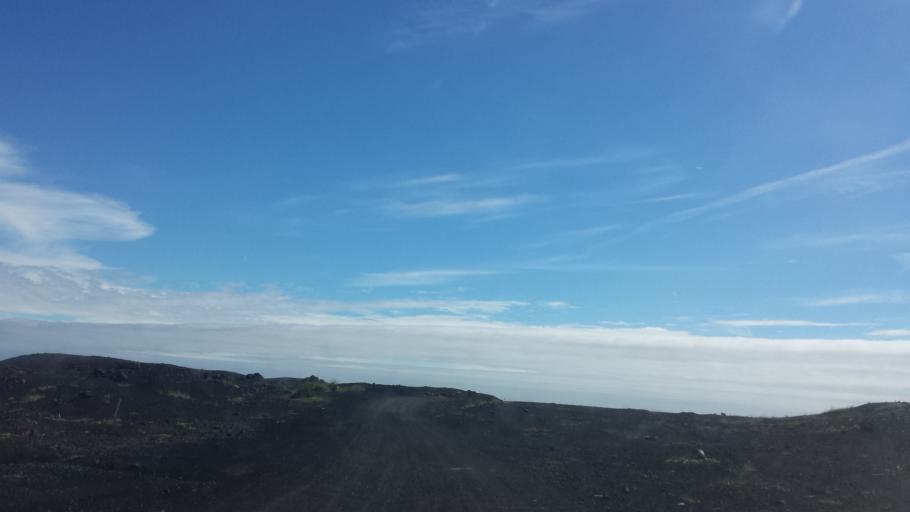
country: IS
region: South
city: Vestmannaeyjar
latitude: 63.4375
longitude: -20.2398
